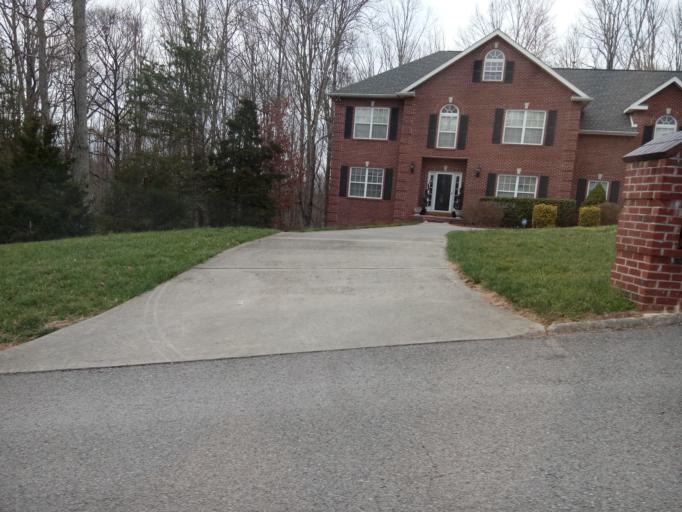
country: US
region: Tennessee
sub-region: Knox County
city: Farragut
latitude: 35.8893
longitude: -84.1287
